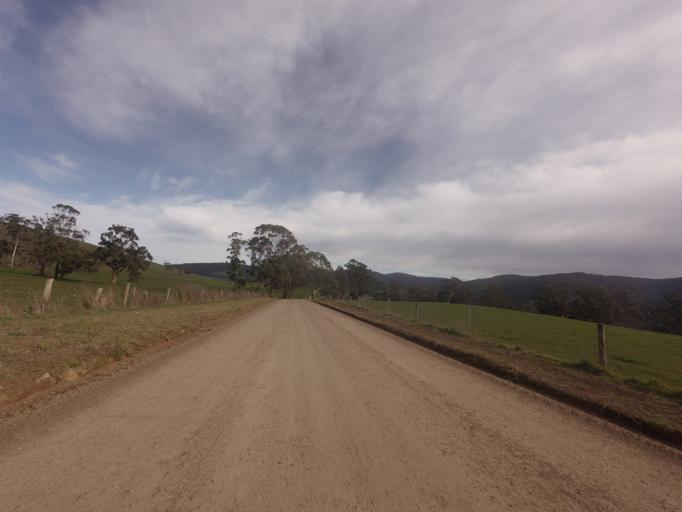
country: AU
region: Tasmania
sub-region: Huon Valley
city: Franklin
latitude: -43.0725
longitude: 147.0468
